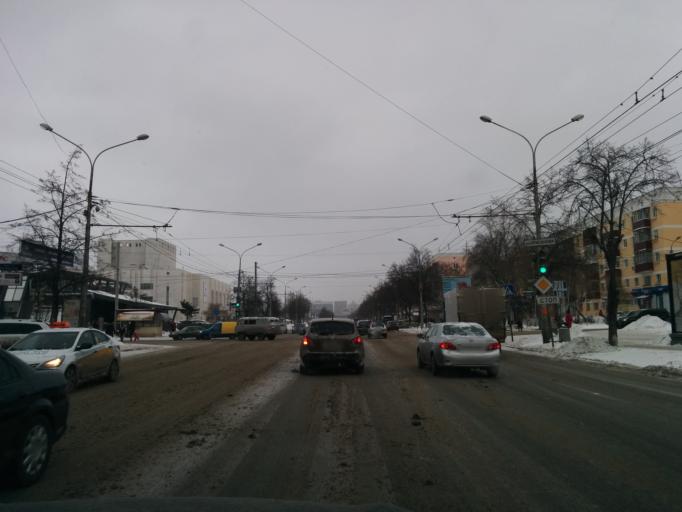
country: RU
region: Perm
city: Perm
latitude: 58.0066
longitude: 56.2119
